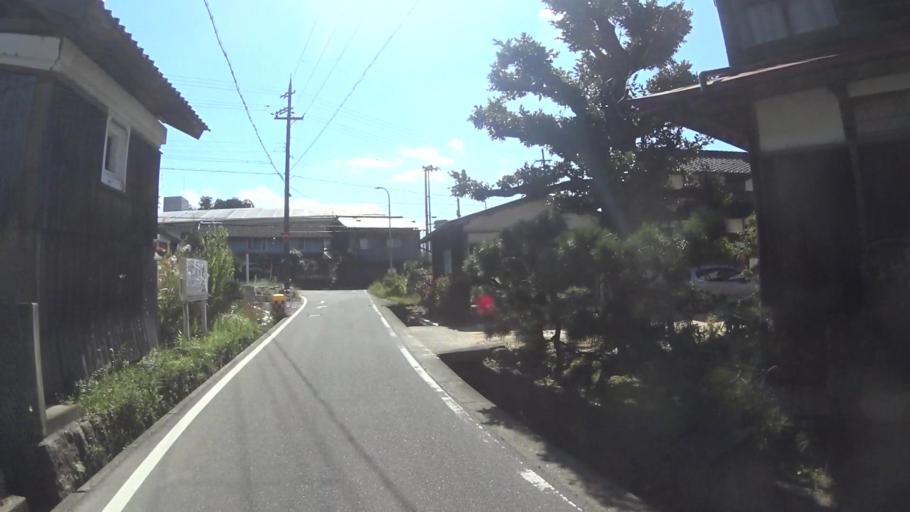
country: JP
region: Hyogo
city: Toyooka
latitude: 35.5906
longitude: 134.9318
